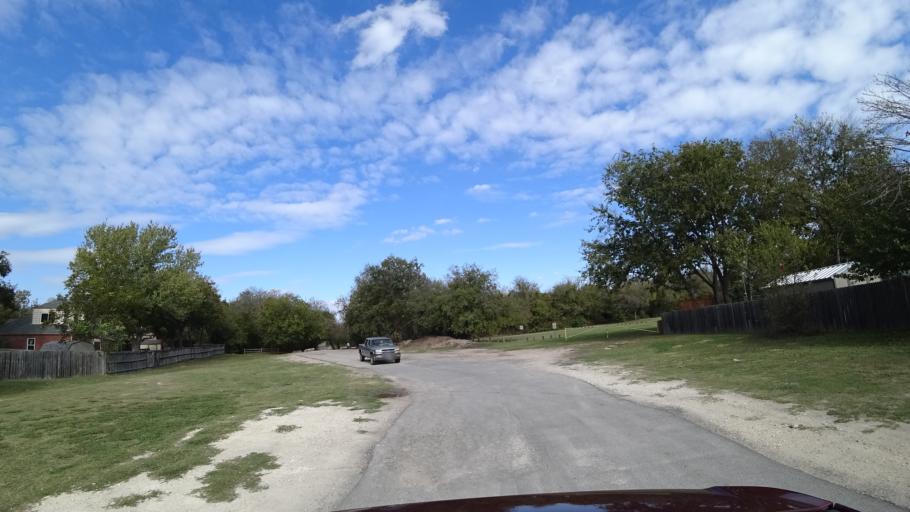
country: US
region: Texas
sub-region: Travis County
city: Pflugerville
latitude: 30.4468
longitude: -97.6244
